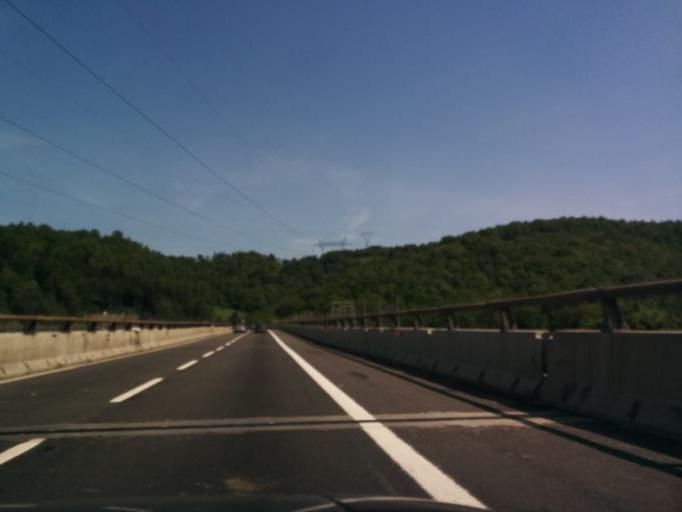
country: IT
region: Tuscany
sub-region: Province of Florence
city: Cavallina
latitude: 43.9382
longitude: 11.2220
